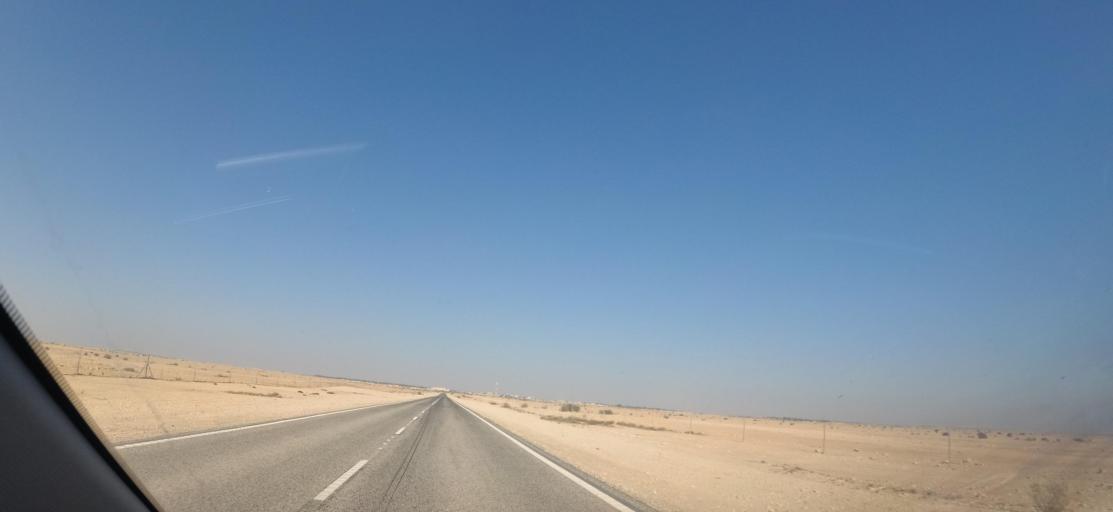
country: QA
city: Al Ghuwayriyah
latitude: 25.8053
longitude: 51.2256
